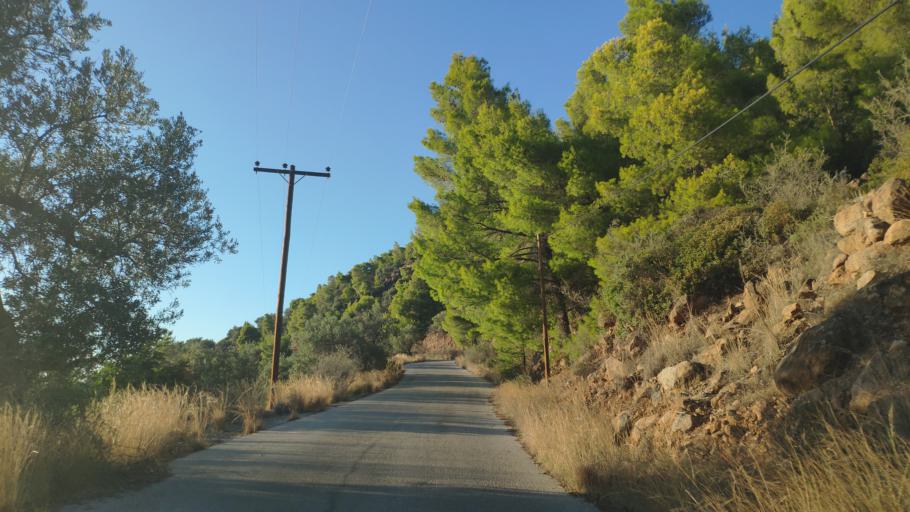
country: GR
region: Attica
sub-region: Nomos Piraios
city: Megalochori
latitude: 37.6011
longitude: 23.3349
